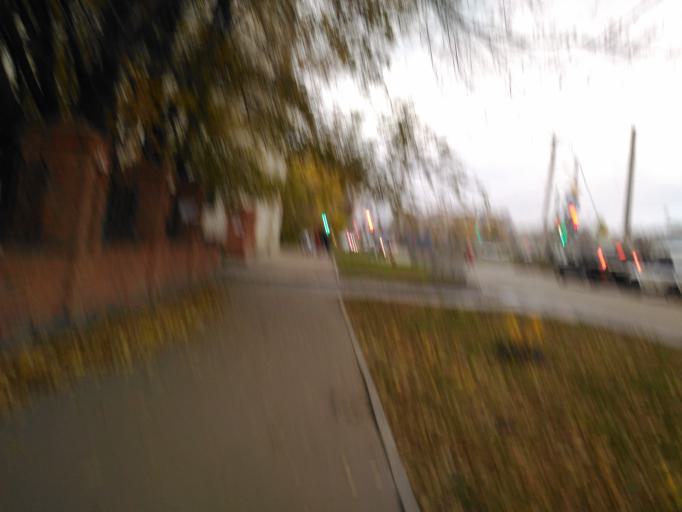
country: RU
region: Ulyanovsk
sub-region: Ulyanovskiy Rayon
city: Ulyanovsk
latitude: 54.3429
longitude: 48.3898
